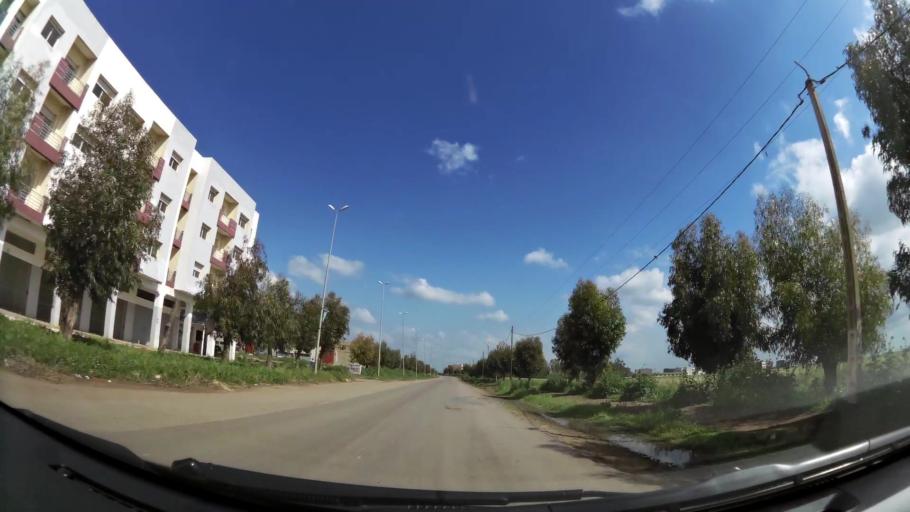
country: MA
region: Grand Casablanca
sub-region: Mediouna
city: Mediouna
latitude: 33.4484
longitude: -7.5060
